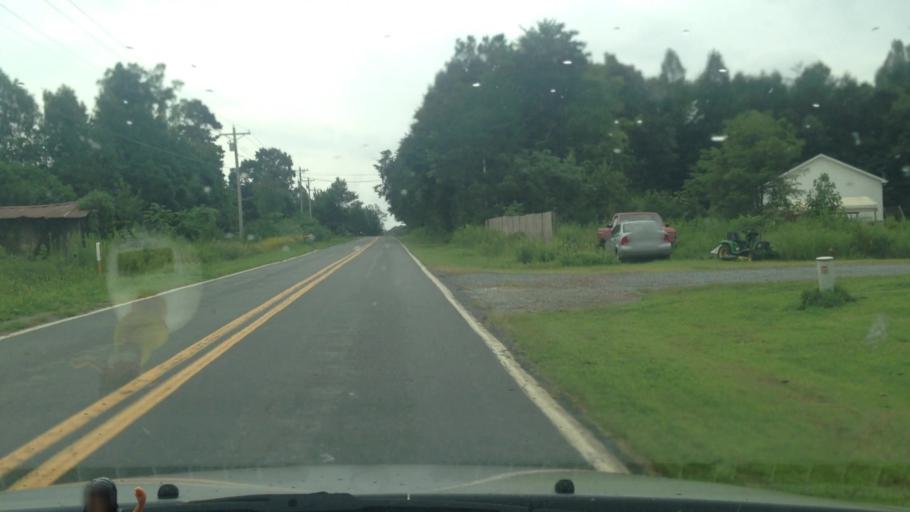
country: US
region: North Carolina
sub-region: Stokes County
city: Danbury
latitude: 36.3888
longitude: -80.1361
